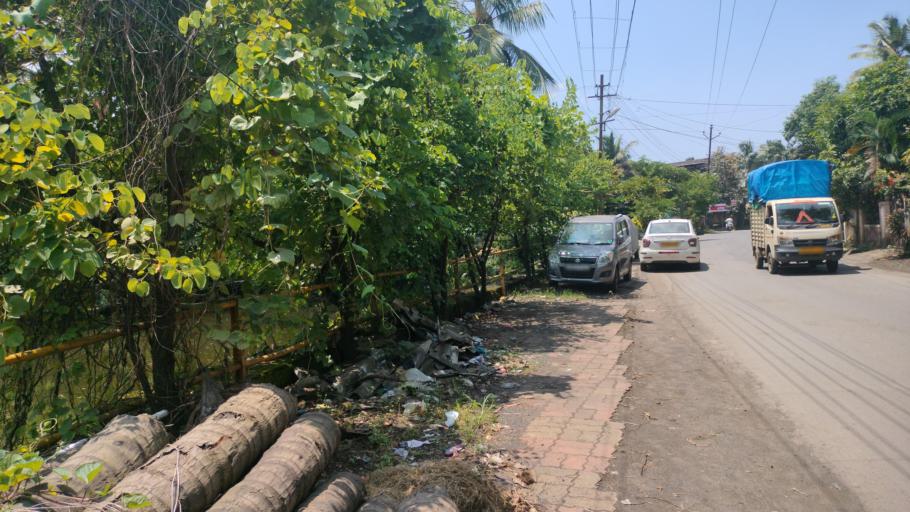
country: IN
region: Maharashtra
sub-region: Thane
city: Virar
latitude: 19.4058
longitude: 72.7988
